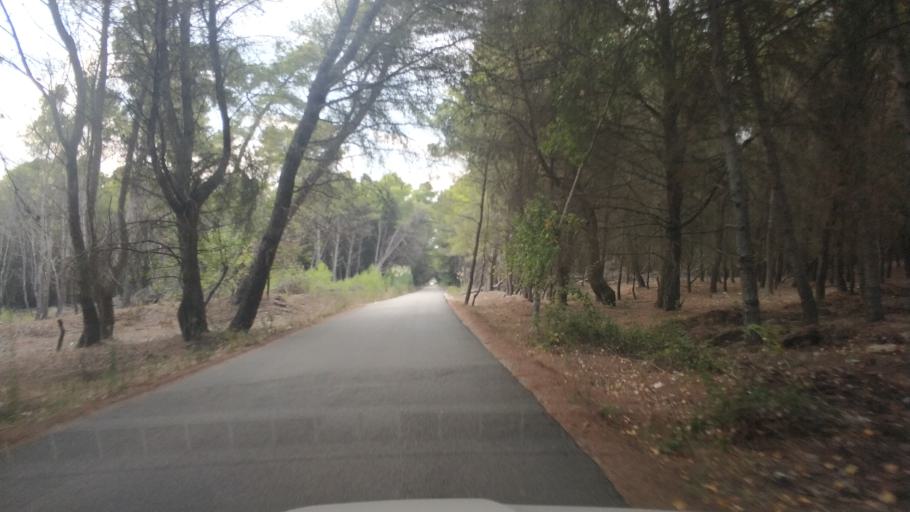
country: AL
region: Vlore
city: Vlore
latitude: 40.4956
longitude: 19.4332
